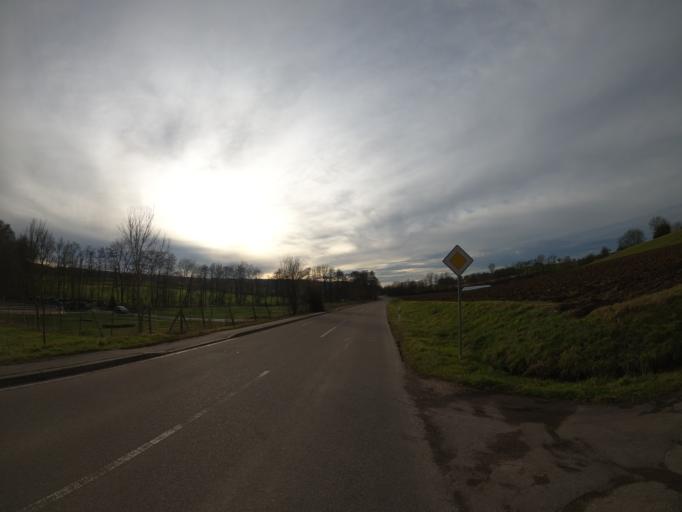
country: DE
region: Baden-Wuerttemberg
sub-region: Regierungsbezirk Stuttgart
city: Birenbach
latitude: 48.7284
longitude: 9.6771
